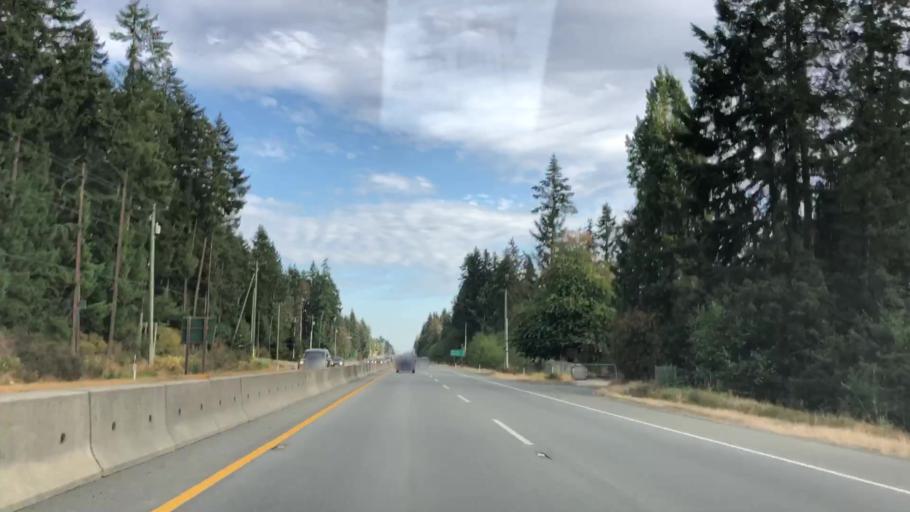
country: CA
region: British Columbia
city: Duncan
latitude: 48.7032
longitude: -123.6017
